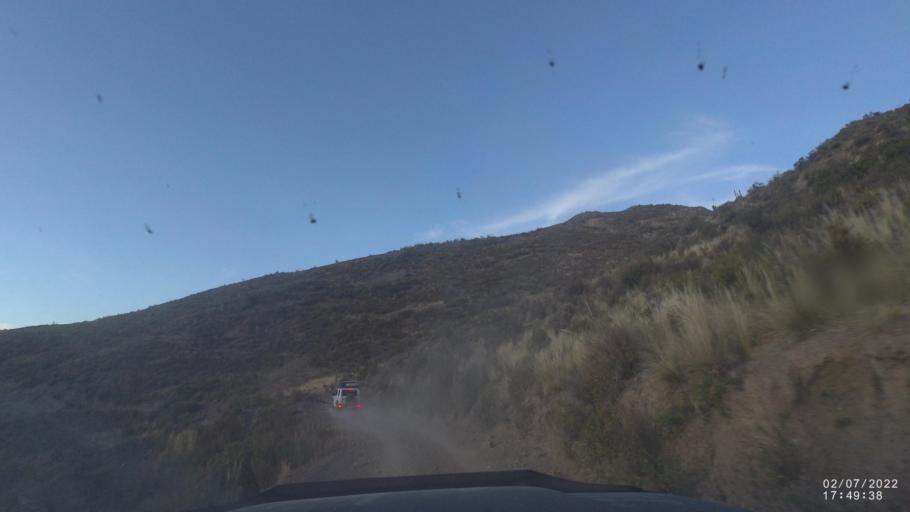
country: BO
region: Cochabamba
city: Irpa Irpa
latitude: -17.8519
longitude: -66.6172
